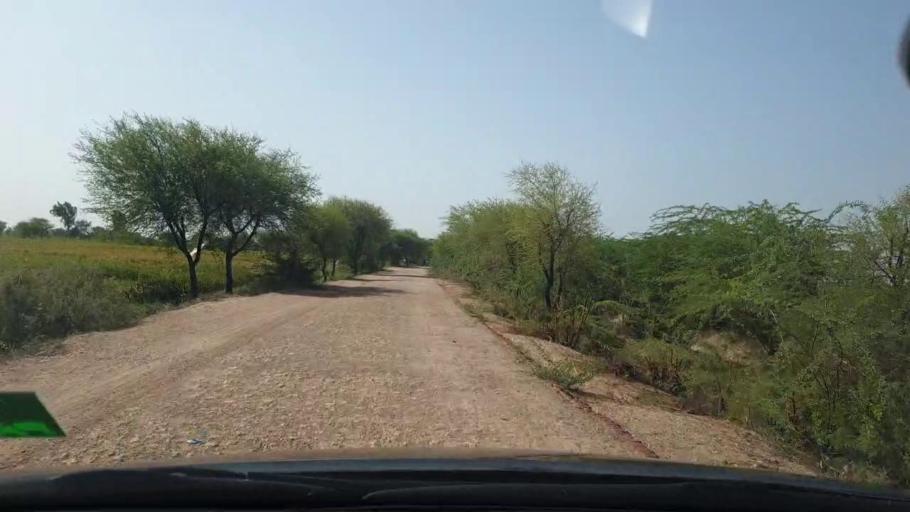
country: PK
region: Sindh
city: Tando Bago
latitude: 24.7490
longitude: 68.9868
